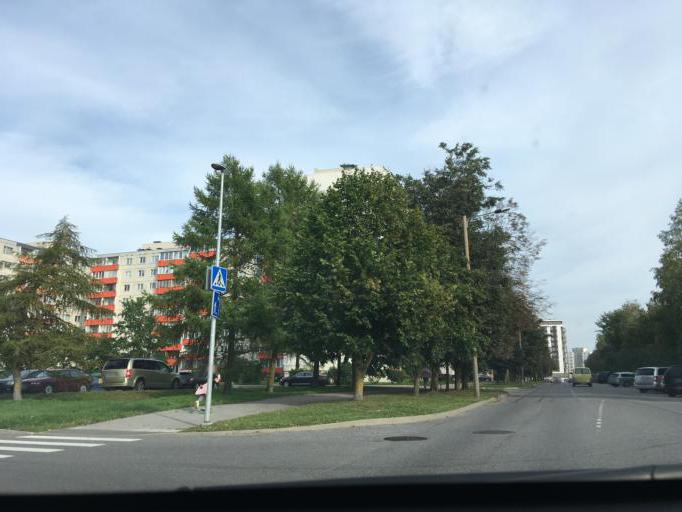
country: EE
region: Harju
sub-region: Tallinna linn
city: Kose
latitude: 59.4494
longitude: 24.8819
